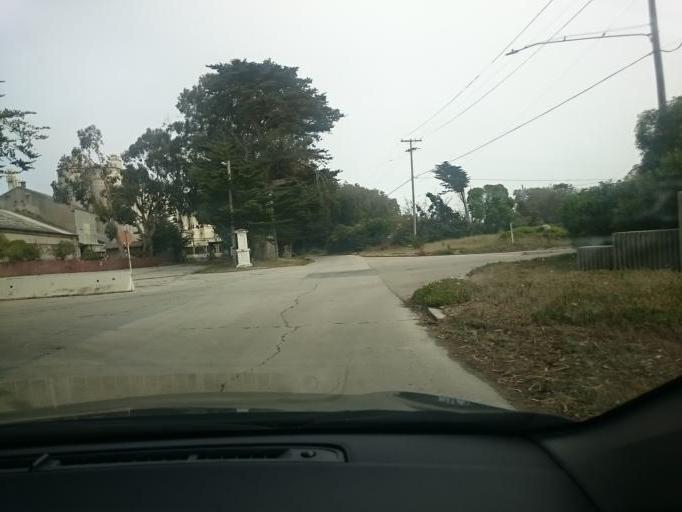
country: US
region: California
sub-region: Santa Cruz County
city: Bonny Doon
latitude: 37.0153
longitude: -122.2008
